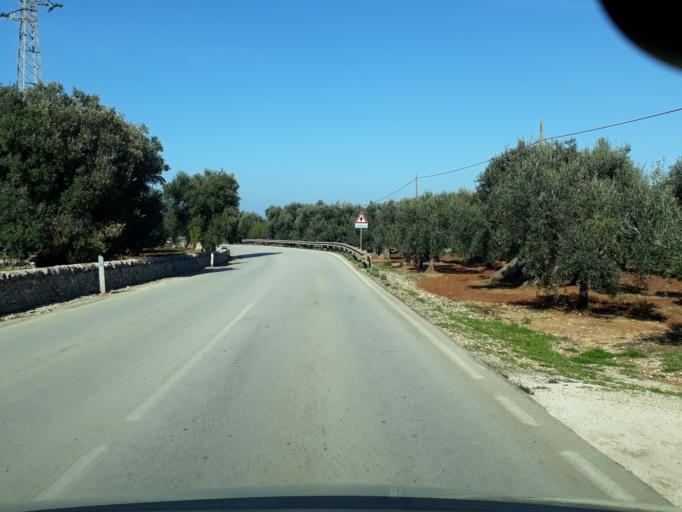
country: IT
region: Apulia
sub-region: Provincia di Bari
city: Monopoli
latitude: 40.9191
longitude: 17.2798
